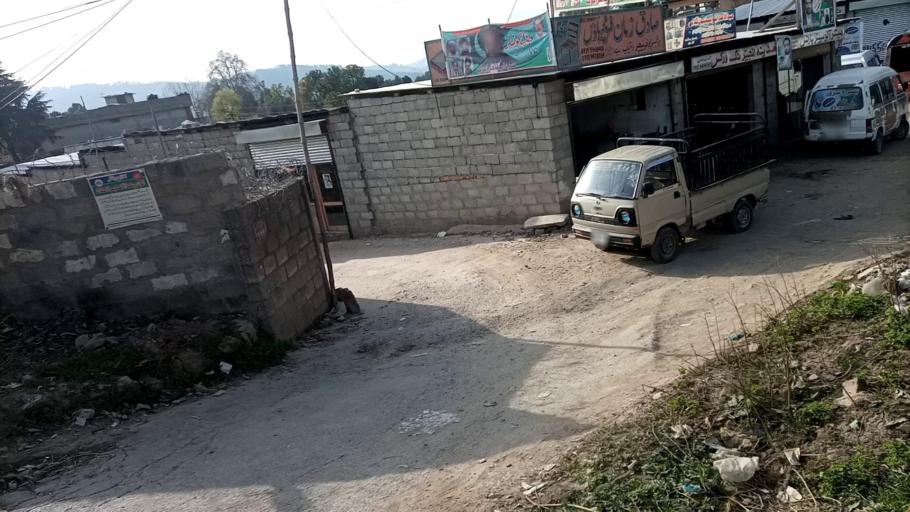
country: PK
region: Khyber Pakhtunkhwa
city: Abbottabad
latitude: 34.2197
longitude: 73.2446
